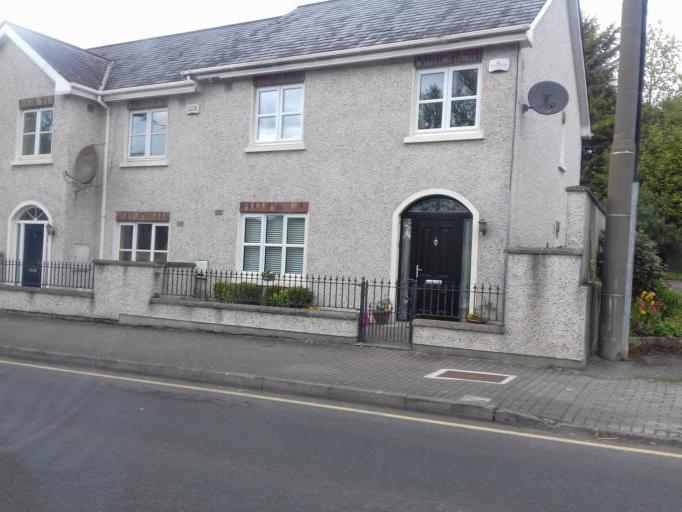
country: IE
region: Leinster
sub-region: Kildare
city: Kildare
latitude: 53.1574
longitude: -6.9149
